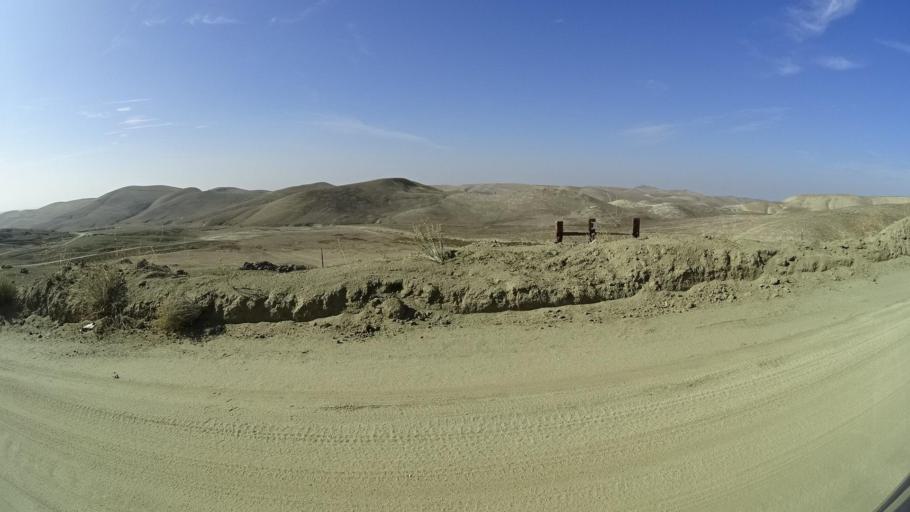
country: US
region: California
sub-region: Kern County
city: Oildale
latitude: 35.4774
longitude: -118.8254
